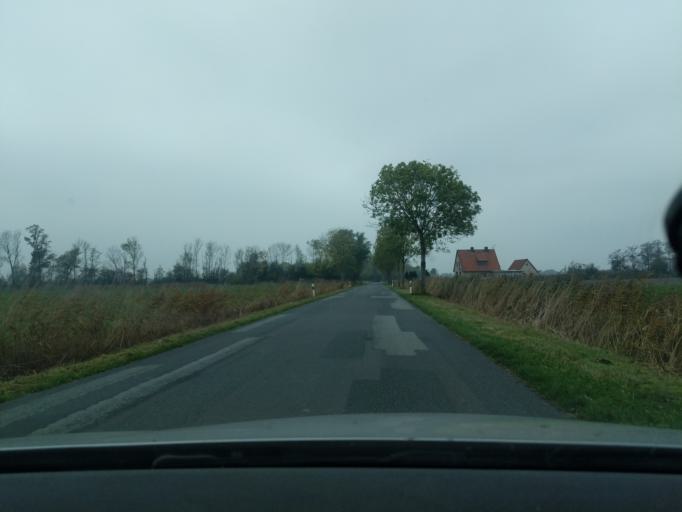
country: DE
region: Lower Saxony
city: Nordleda
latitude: 53.8249
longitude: 8.7947
